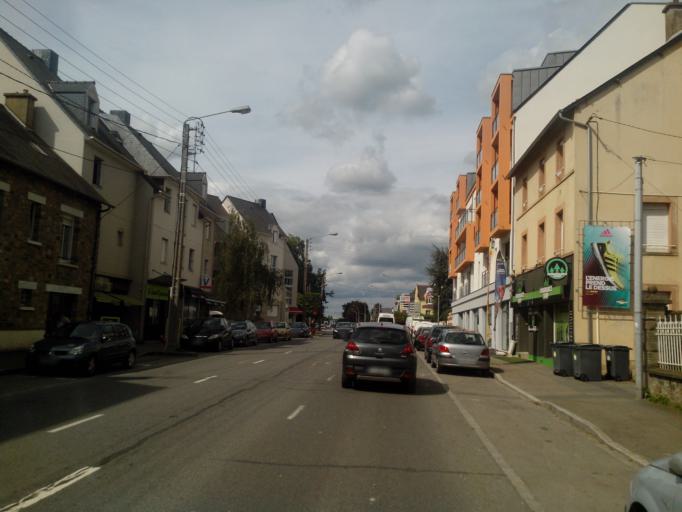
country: FR
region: Brittany
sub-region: Departement d'Ille-et-Vilaine
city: Rennes
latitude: 48.1249
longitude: -1.6852
